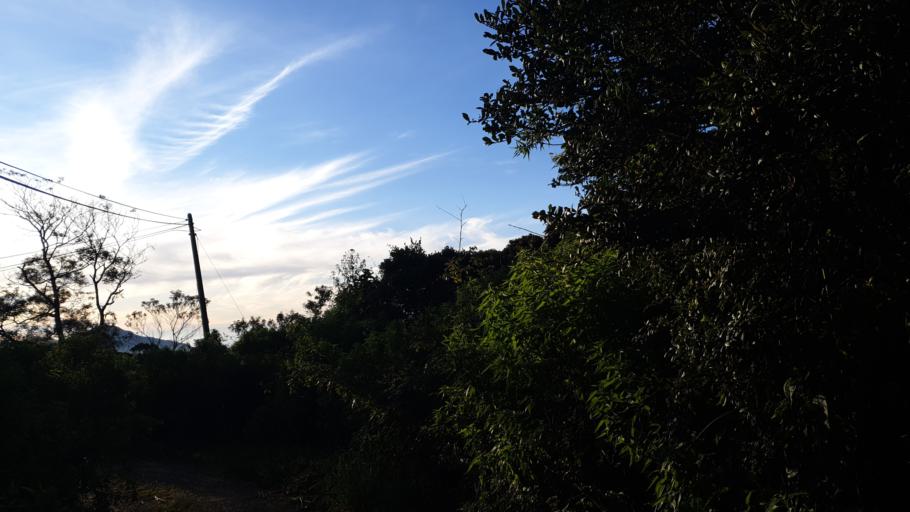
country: LK
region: Central
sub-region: Nuwara Eliya District
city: Nuwara Eliya
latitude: 6.9569
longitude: 80.7625
